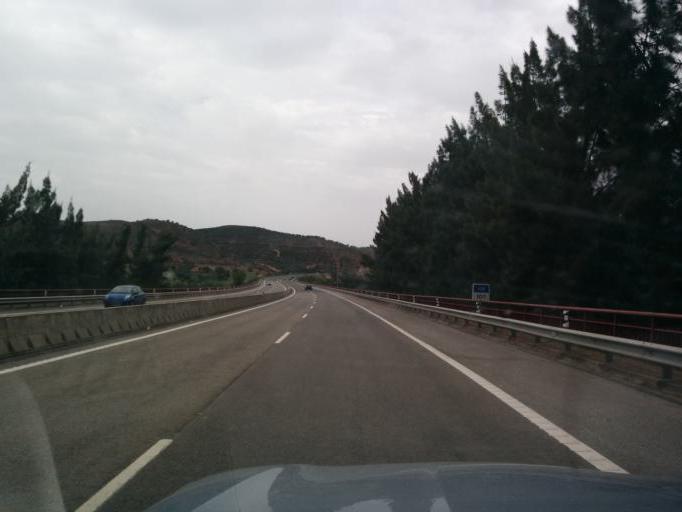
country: PT
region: Faro
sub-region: Tavira
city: Tavira
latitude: 37.1520
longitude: -7.6684
